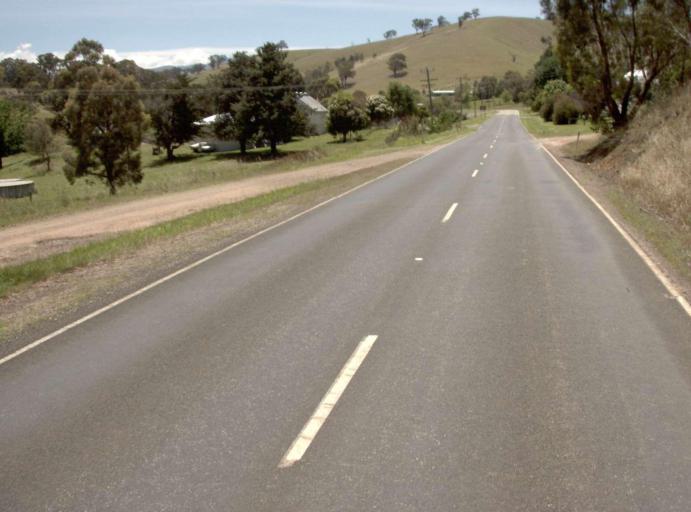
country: AU
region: Victoria
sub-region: East Gippsland
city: Bairnsdale
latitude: -37.3770
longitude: 147.8331
